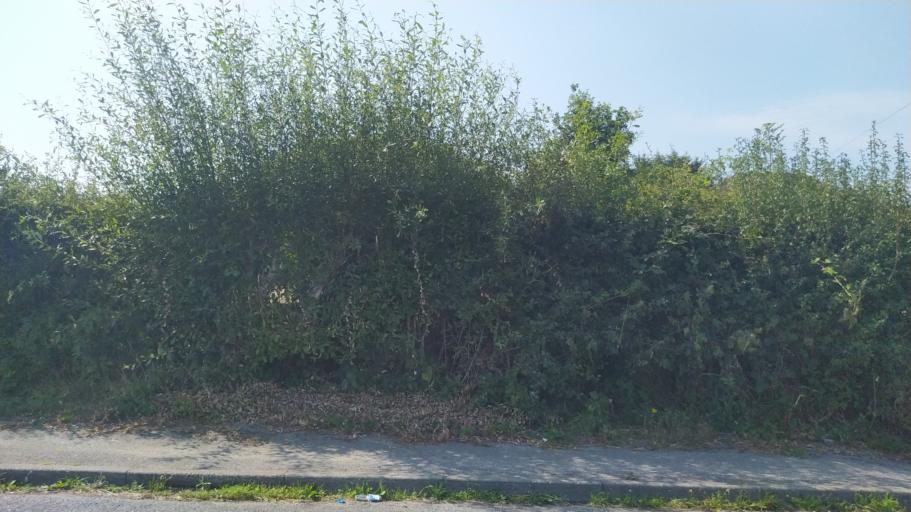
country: GB
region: England
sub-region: Hampshire
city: Totton
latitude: 50.9121
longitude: -1.5317
